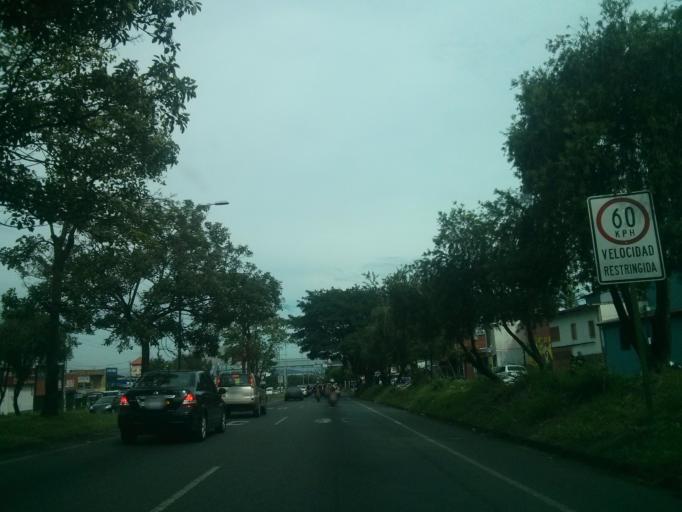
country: CR
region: San Jose
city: San Felipe
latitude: 9.9246
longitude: -84.1101
